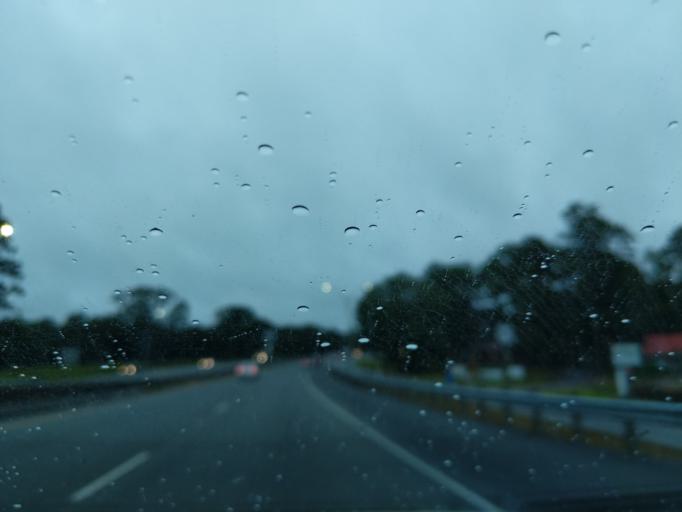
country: US
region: Texas
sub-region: Angelina County
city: Lufkin
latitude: 31.3206
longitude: -94.6984
